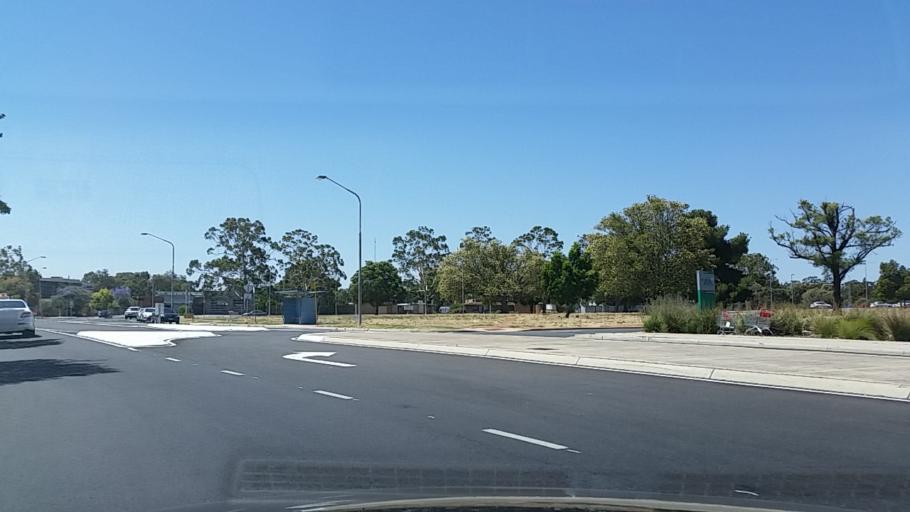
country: AU
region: South Australia
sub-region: Salisbury
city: Elizabeth
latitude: -34.7165
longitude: 138.6716
